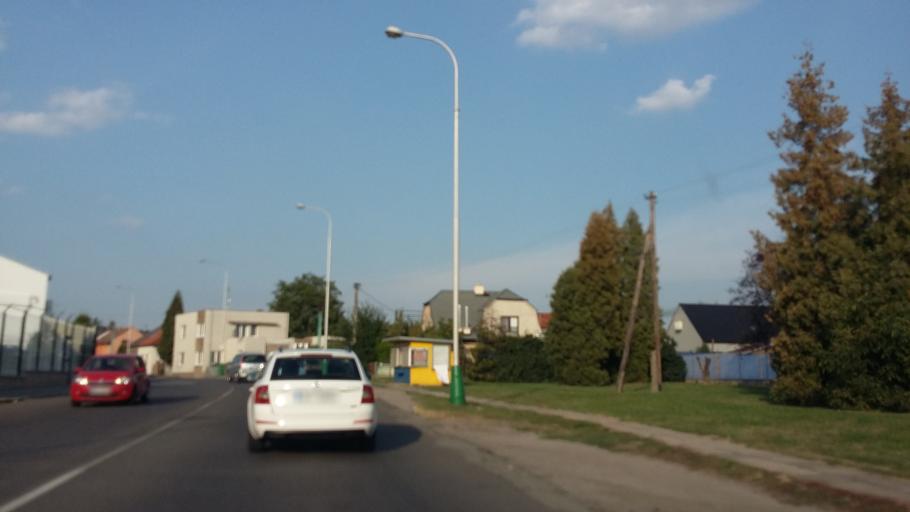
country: CZ
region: Central Bohemia
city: Kosmonosy
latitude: 50.4339
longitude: 14.9269
